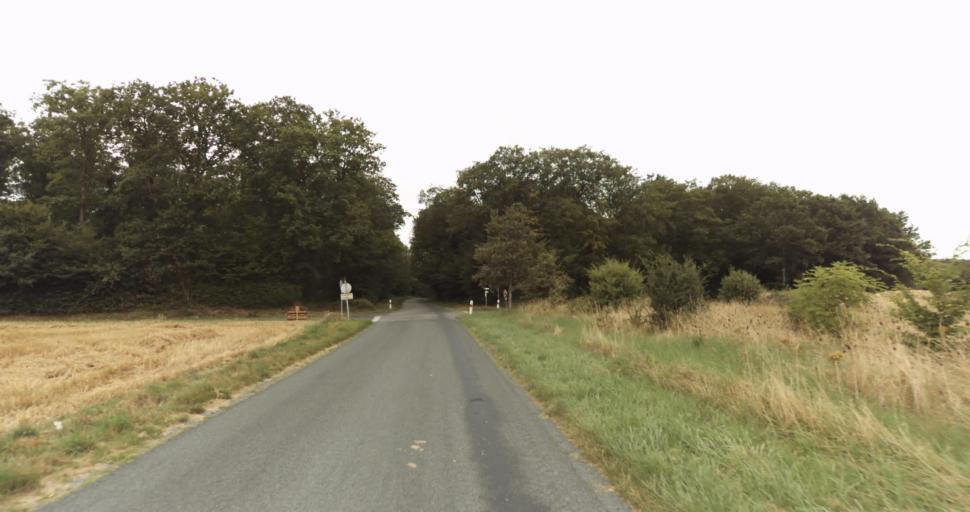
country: FR
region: Centre
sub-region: Departement d'Eure-et-Loir
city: Saint-Remy-sur-Avre
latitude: 48.7787
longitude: 1.2434
